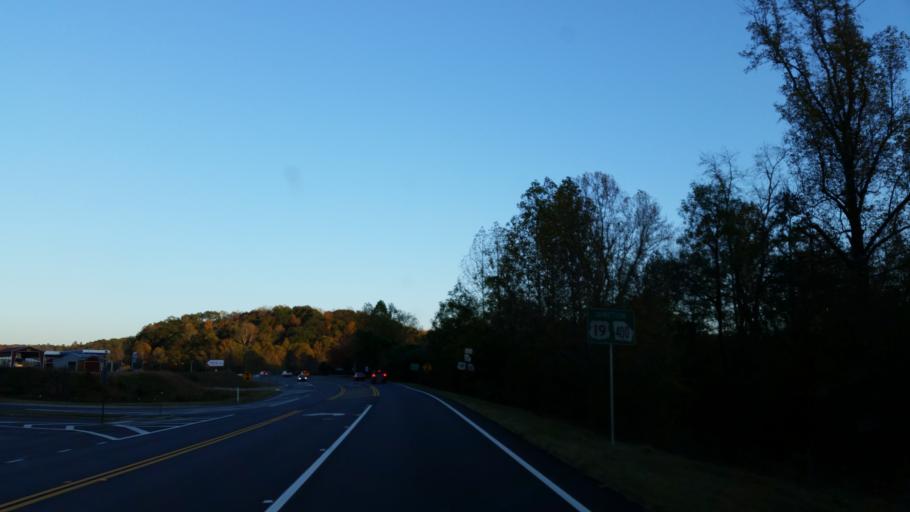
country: US
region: Georgia
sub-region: Lumpkin County
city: Dahlonega
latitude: 34.4690
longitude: -83.9716
